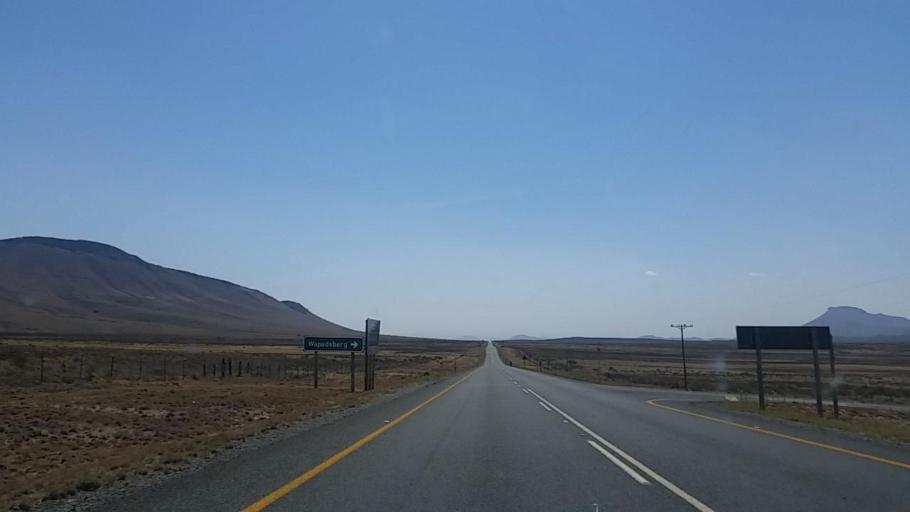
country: ZA
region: Eastern Cape
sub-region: Chris Hani District Municipality
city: Middelburg
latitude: -31.7674
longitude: 24.9152
